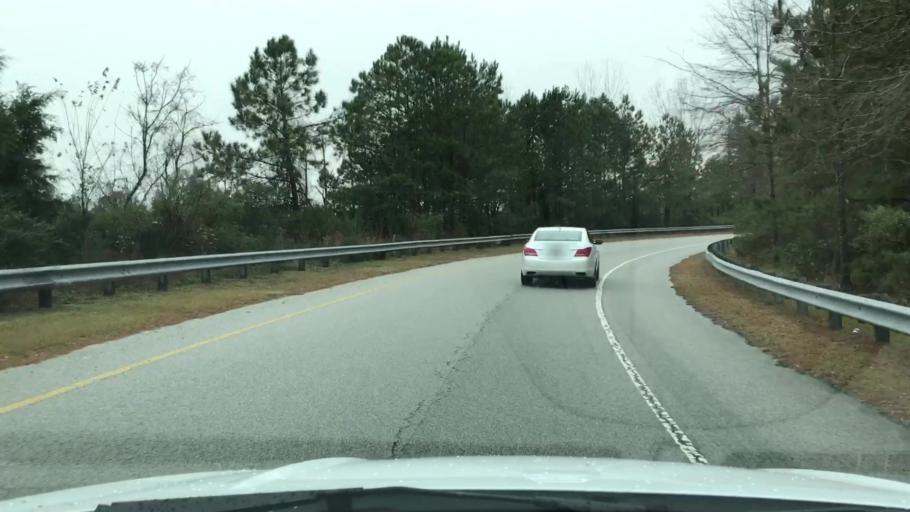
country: US
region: South Carolina
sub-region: Horry County
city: Myrtle Beach
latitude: 33.7402
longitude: -78.8493
